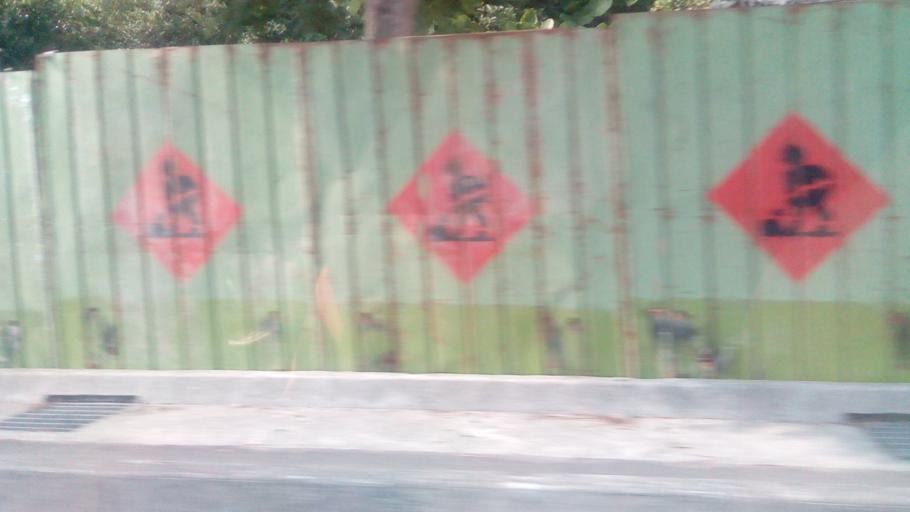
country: TW
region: Taiwan
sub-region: Yilan
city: Yilan
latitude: 24.5880
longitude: 121.8624
